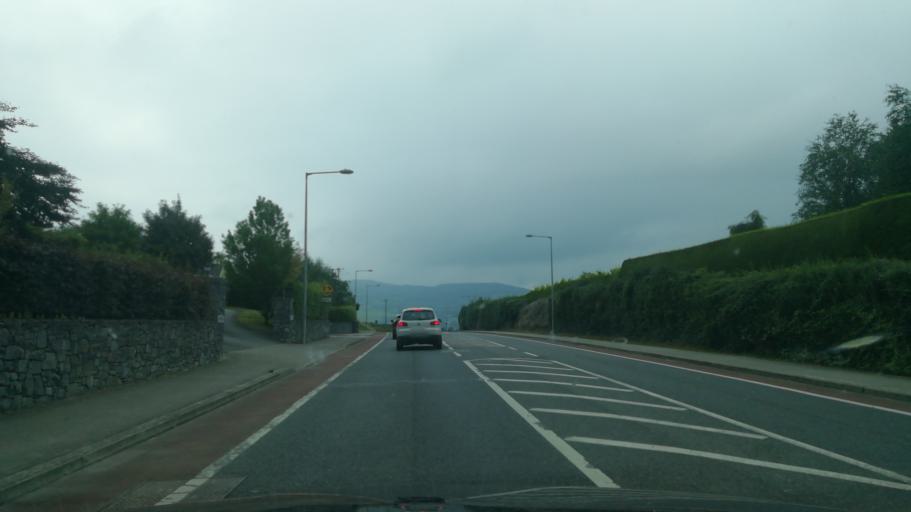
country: IE
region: Munster
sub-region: South Tipperary
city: Cluain Meala
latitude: 52.3707
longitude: -7.6996
